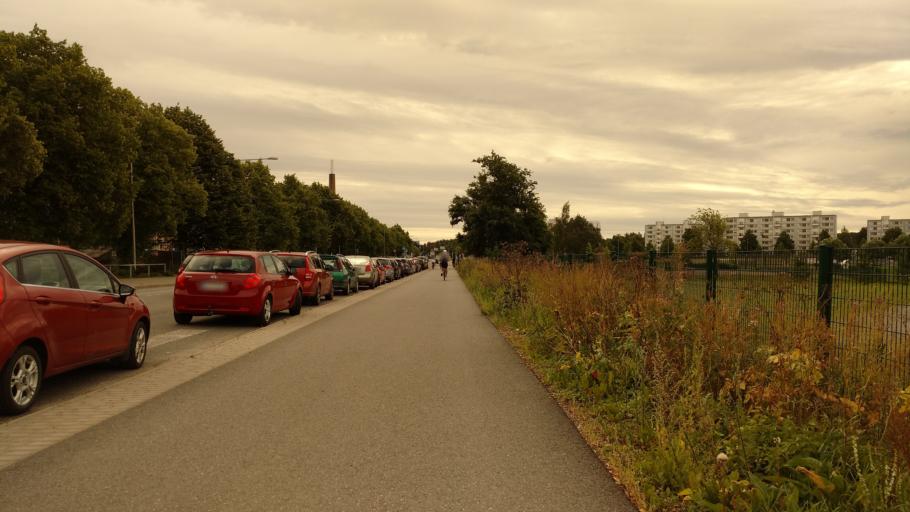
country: FI
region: Varsinais-Suomi
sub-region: Turku
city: Turku
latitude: 60.4465
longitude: 22.2986
